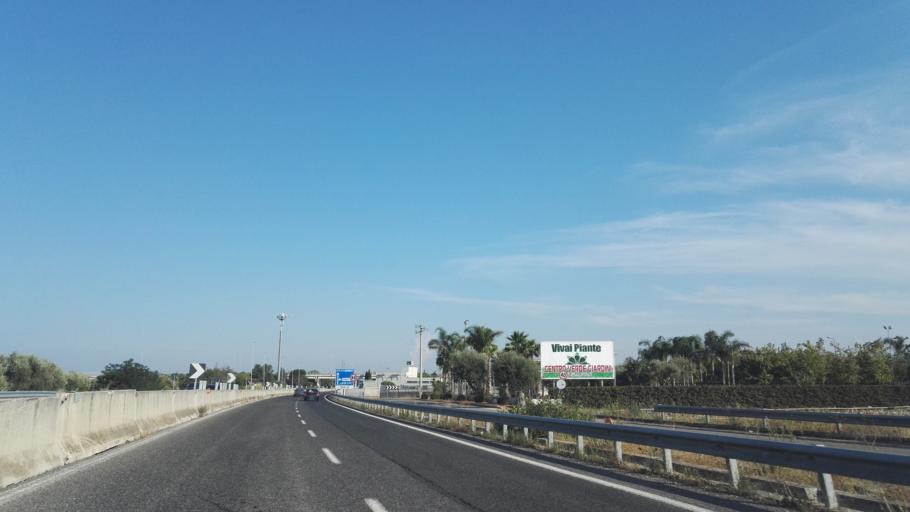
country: IT
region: Apulia
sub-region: Provincia di Bari
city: Monopoli
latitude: 40.9249
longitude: 17.3124
